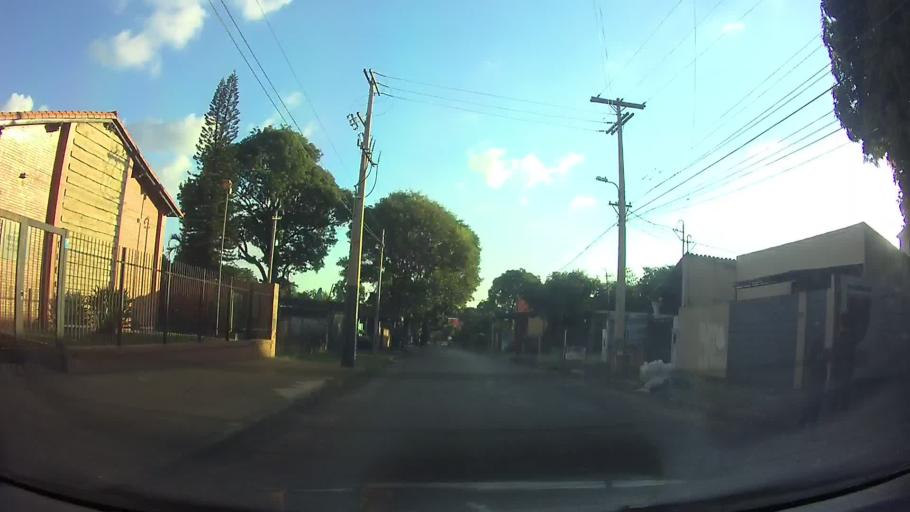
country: PY
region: Central
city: Lambare
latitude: -25.3219
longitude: -57.5717
